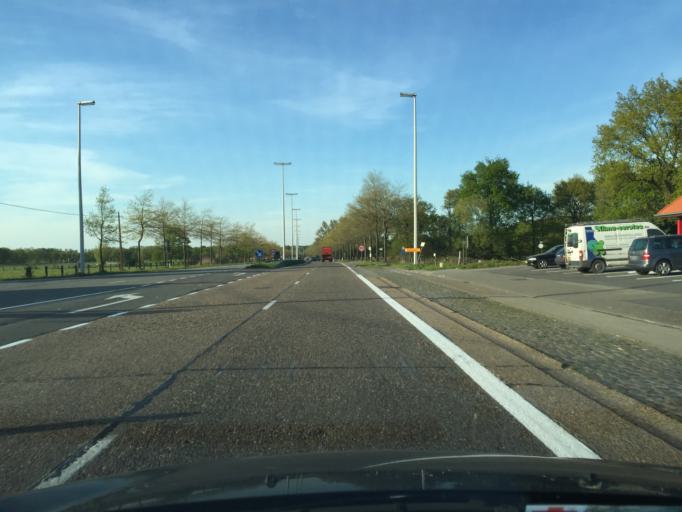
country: BE
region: Flanders
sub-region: Provincie Oost-Vlaanderen
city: Knesselare
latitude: 51.1534
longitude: 3.4330
